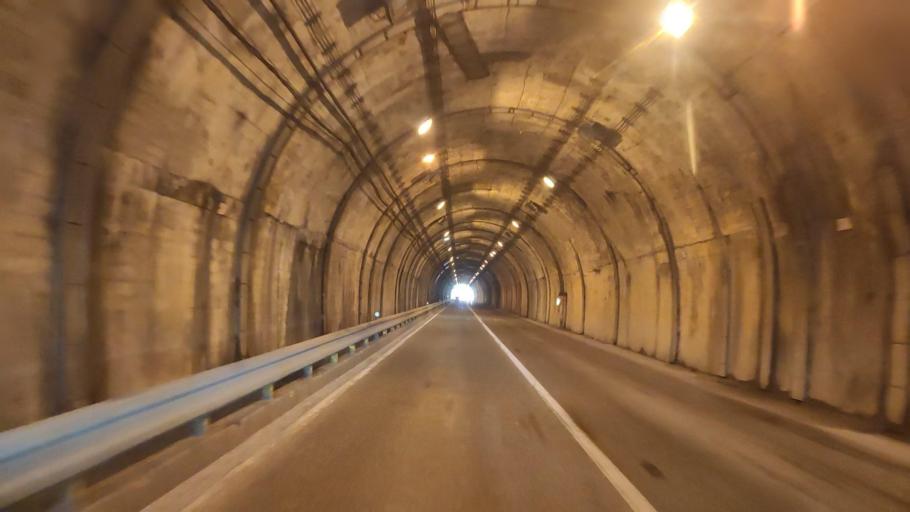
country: JP
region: Fukui
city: Tsuruga
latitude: 35.6625
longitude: 136.0786
